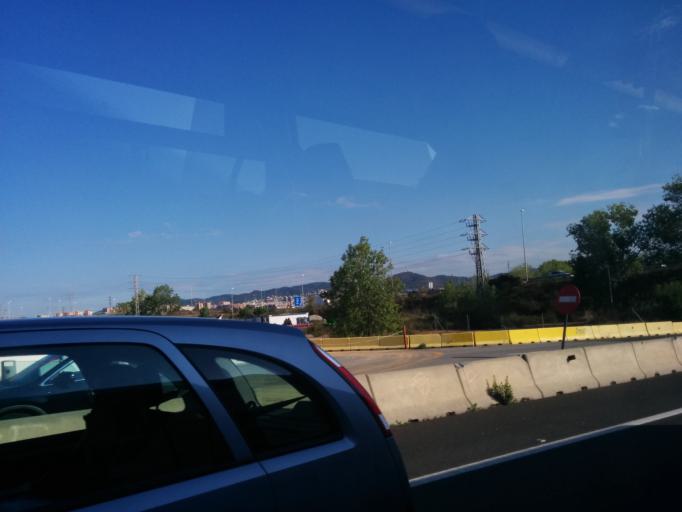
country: ES
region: Catalonia
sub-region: Provincia de Barcelona
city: El Prat de Llobregat
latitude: 41.3386
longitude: 2.1002
